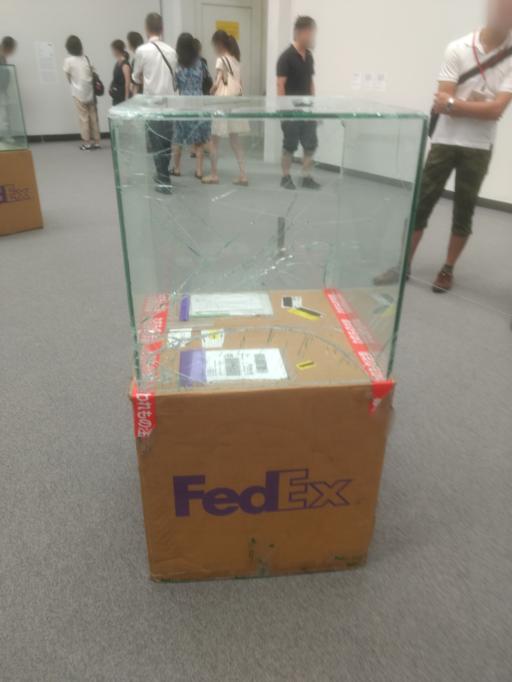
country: JP
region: Aichi
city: Nagoya-shi
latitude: 35.1711
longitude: 136.9116
